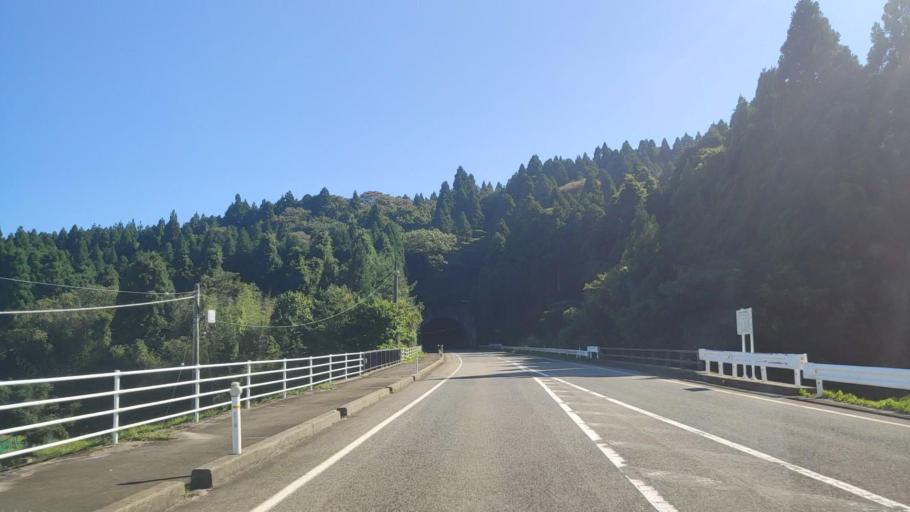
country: JP
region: Ishikawa
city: Nanao
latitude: 37.3859
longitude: 137.2330
